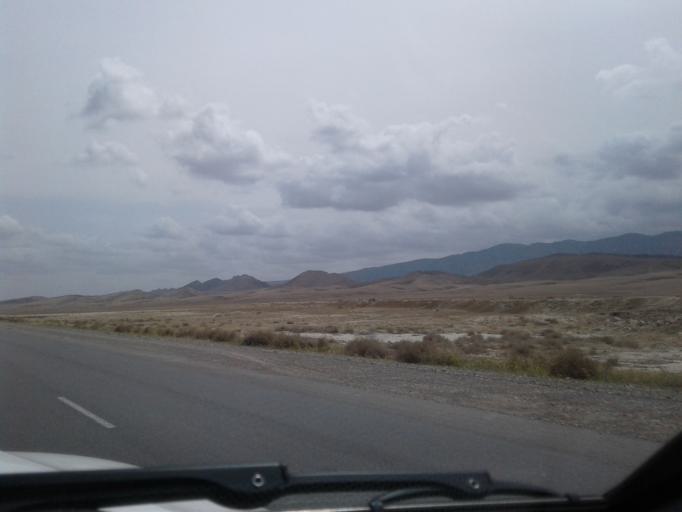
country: IR
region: Razavi Khorasan
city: Dargaz
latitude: 37.7023
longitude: 59.0403
